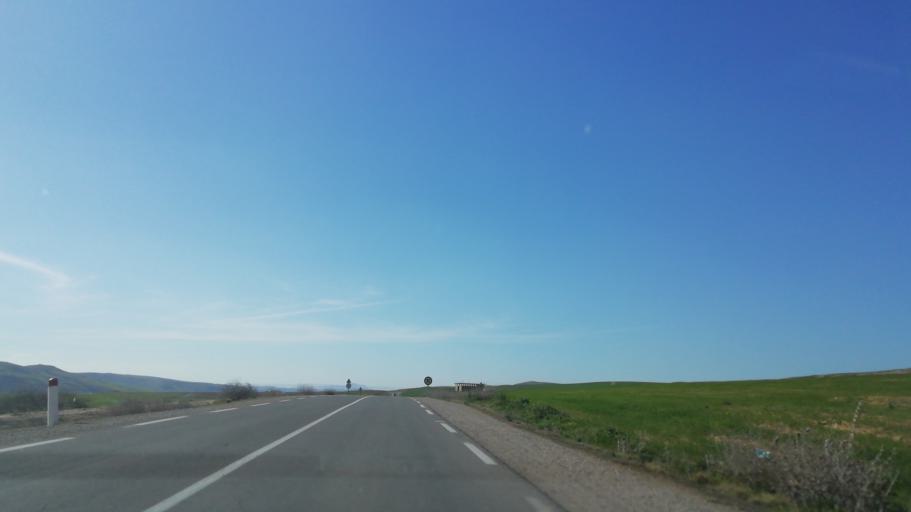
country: DZ
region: Mascara
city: Oued el Abtal
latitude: 35.4446
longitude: 0.8268
